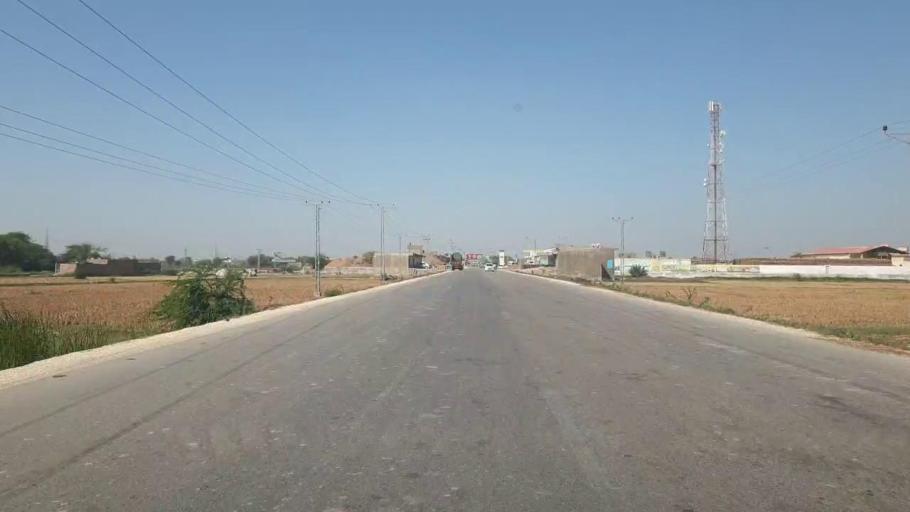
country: PK
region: Sindh
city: Talhar
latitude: 24.8805
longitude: 68.8118
